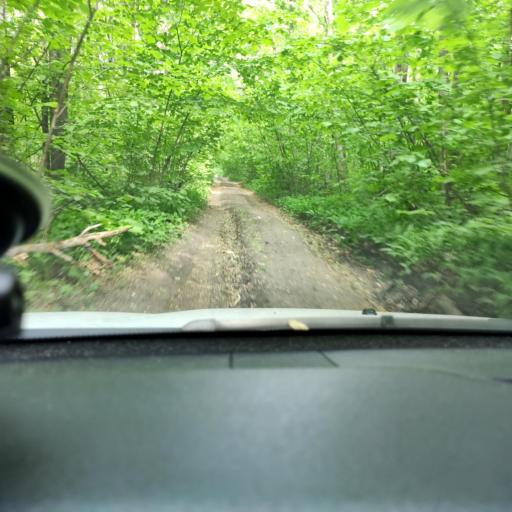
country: RU
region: Samara
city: Novosemeykino
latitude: 53.3177
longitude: 50.2263
